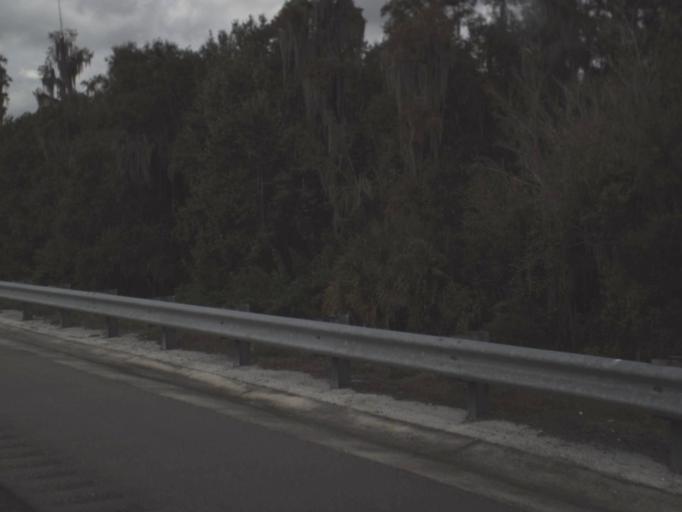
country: US
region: Florida
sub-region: Polk County
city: Fussels Corner
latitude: 28.0110
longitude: -81.8504
